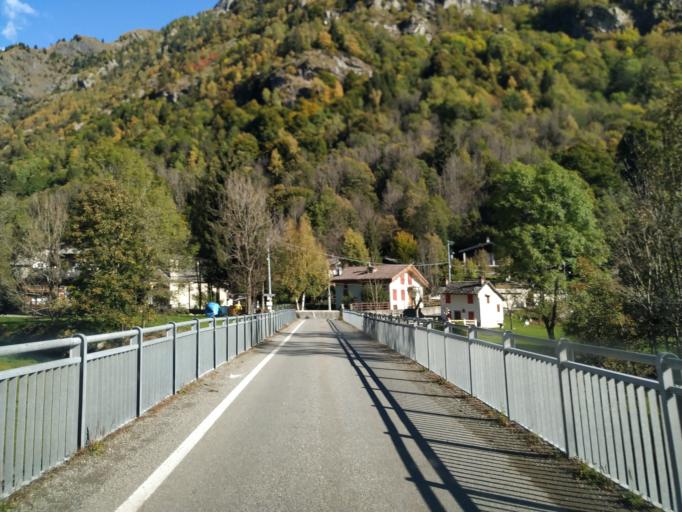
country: IT
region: Piedmont
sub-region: Provincia di Vercelli
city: Riva Valdobbia
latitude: 45.8374
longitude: 7.9517
